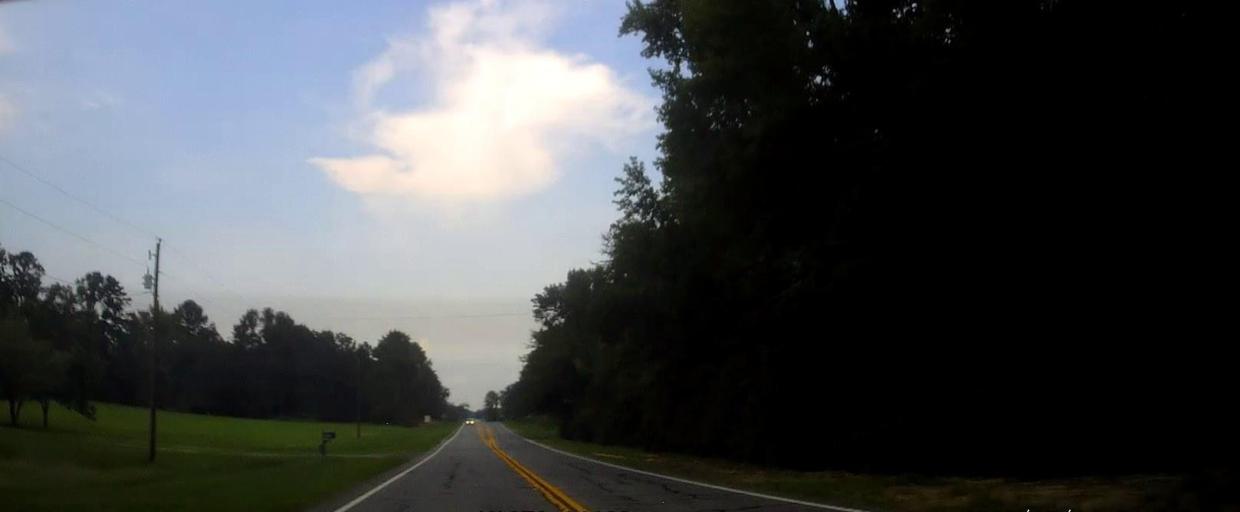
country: US
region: Georgia
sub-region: Laurens County
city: East Dublin
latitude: 32.6031
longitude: -82.8223
